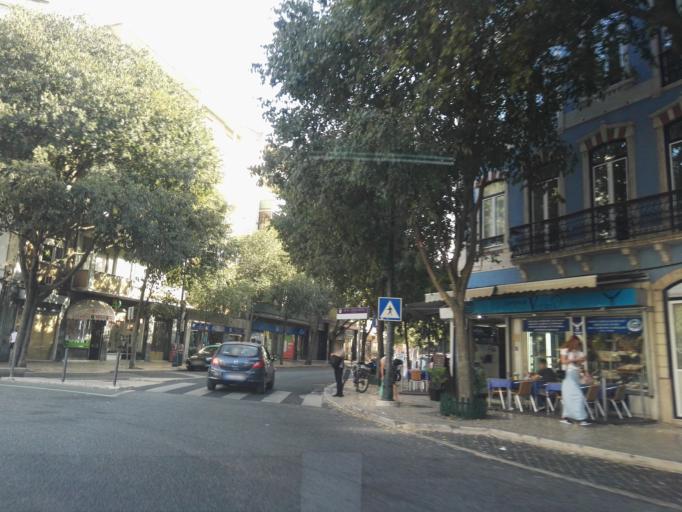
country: PT
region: Lisbon
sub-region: Lisbon
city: Lisbon
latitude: 38.7315
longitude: -9.1410
